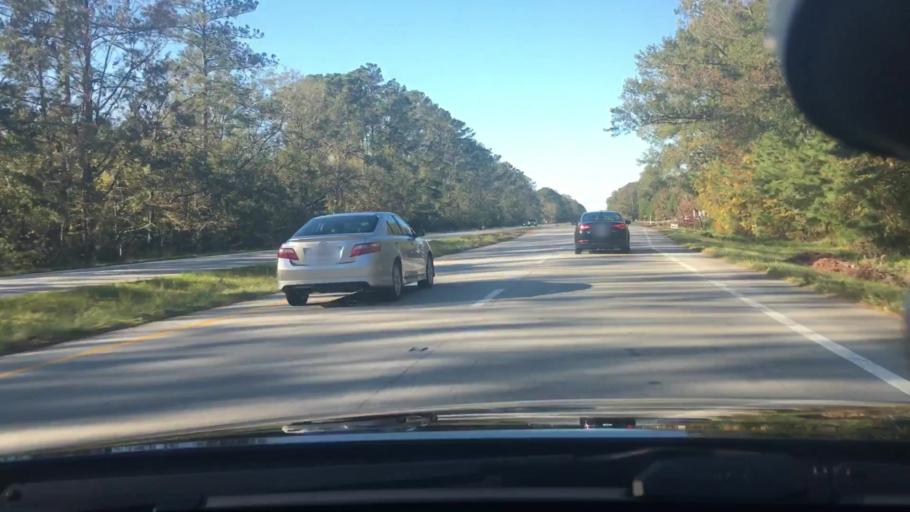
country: US
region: North Carolina
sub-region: Craven County
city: Fairfield Harbour
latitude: 35.0199
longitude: -76.9973
